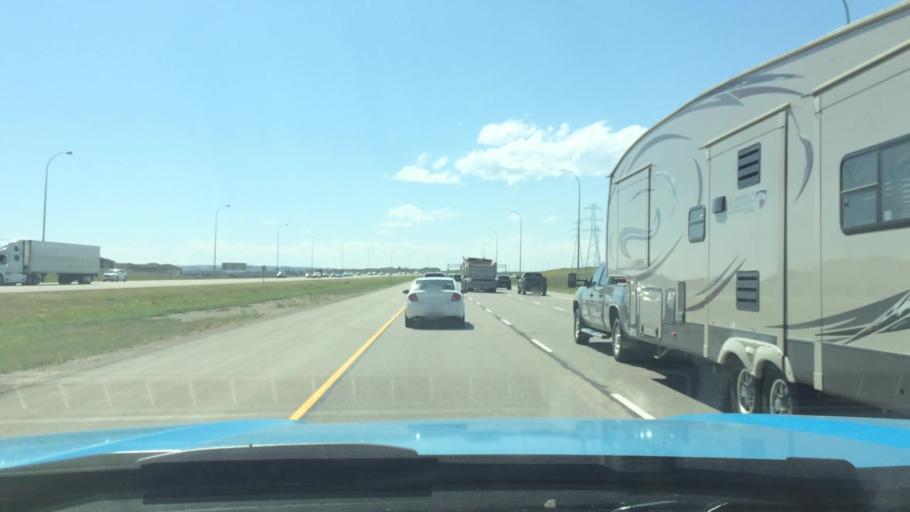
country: CA
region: Alberta
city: Airdrie
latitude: 51.1748
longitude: -114.0502
